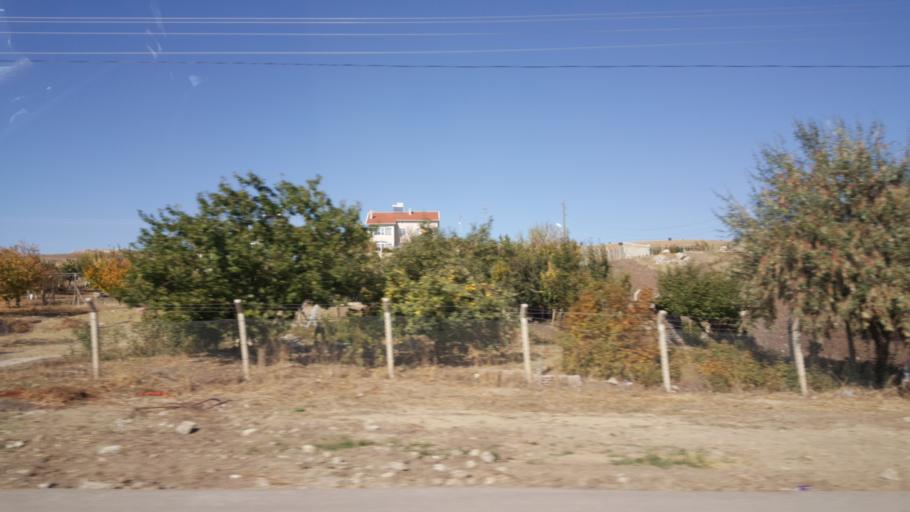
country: TR
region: Ankara
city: Ikizce
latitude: 39.5407
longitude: 32.6285
